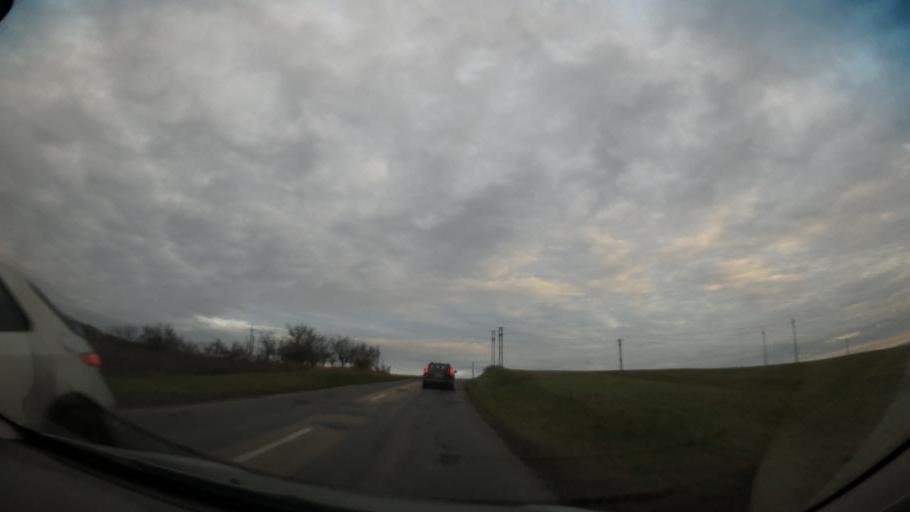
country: CZ
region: South Moravian
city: Oslavany
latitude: 49.1329
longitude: 16.3580
